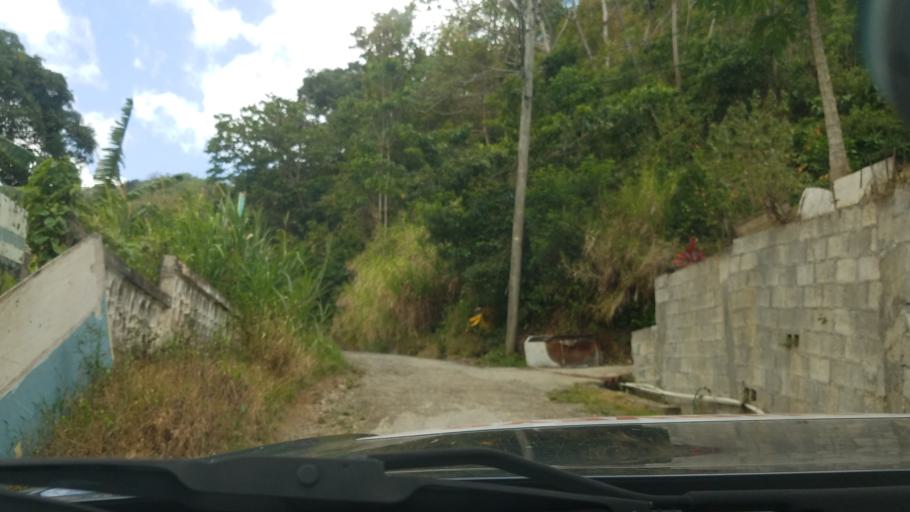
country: LC
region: Gros-Islet
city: Gros Islet
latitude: 14.0589
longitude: -60.9549
